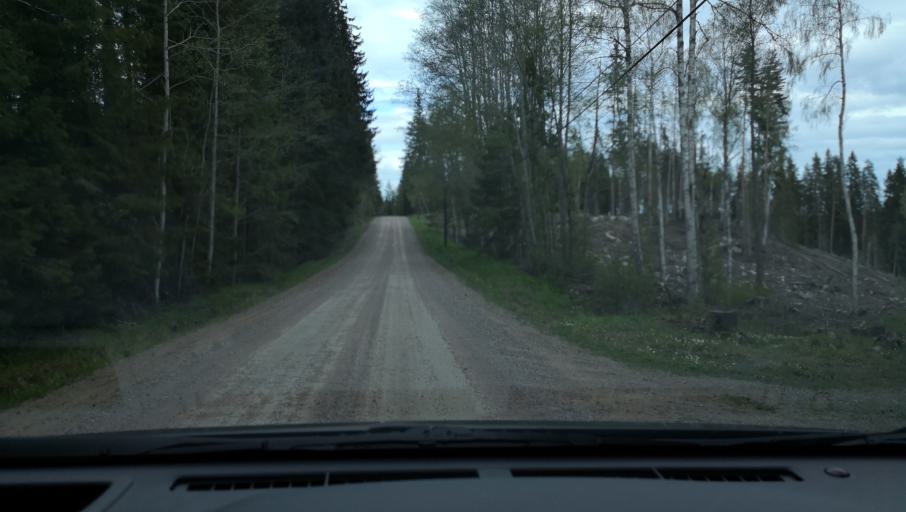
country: SE
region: Vaestmanland
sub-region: Fagersta Kommun
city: Fagersta
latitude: 60.1085
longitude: 15.7970
